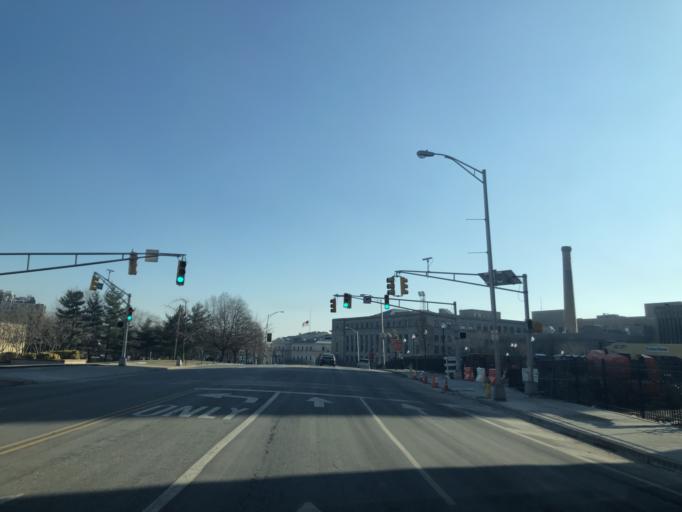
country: US
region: New Jersey
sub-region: Essex County
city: Newark
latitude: 40.7393
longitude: -74.1812
